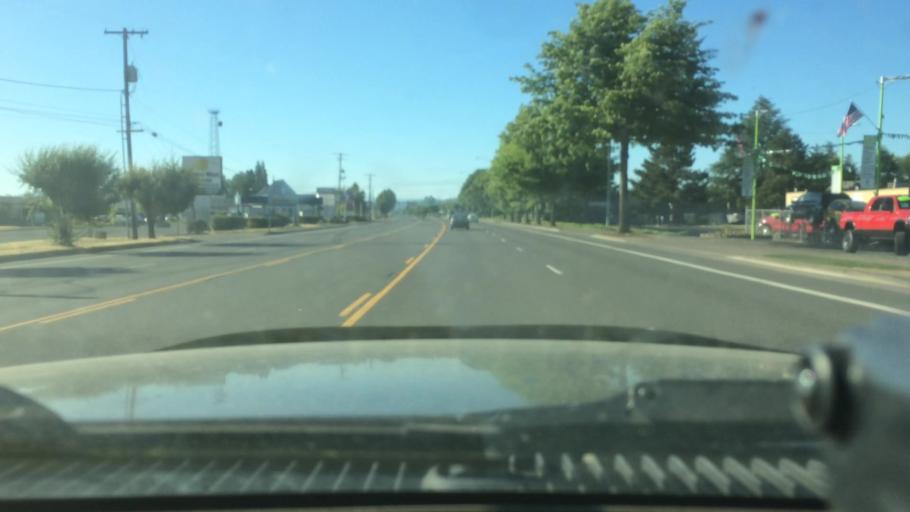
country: US
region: Oregon
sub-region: Lane County
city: Eugene
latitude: 44.0775
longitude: -123.1495
